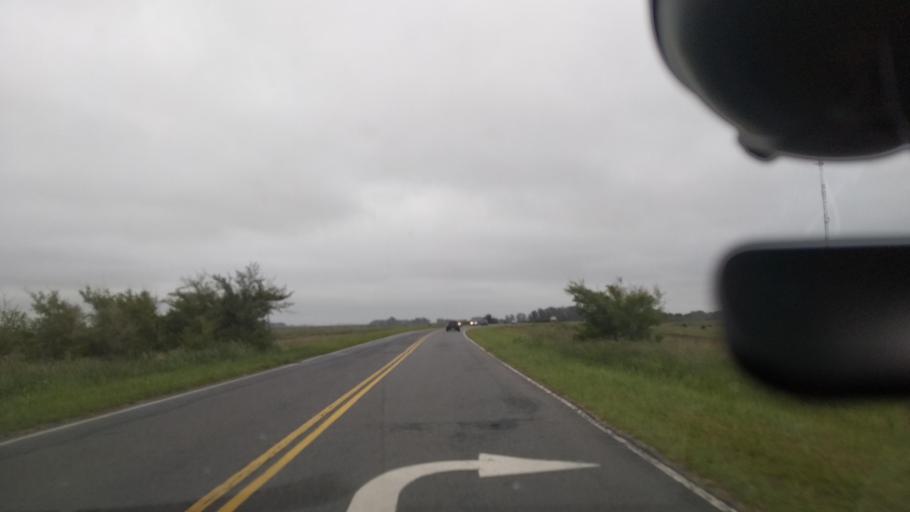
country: AR
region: Buenos Aires
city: Veronica
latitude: -35.4427
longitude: -57.3414
